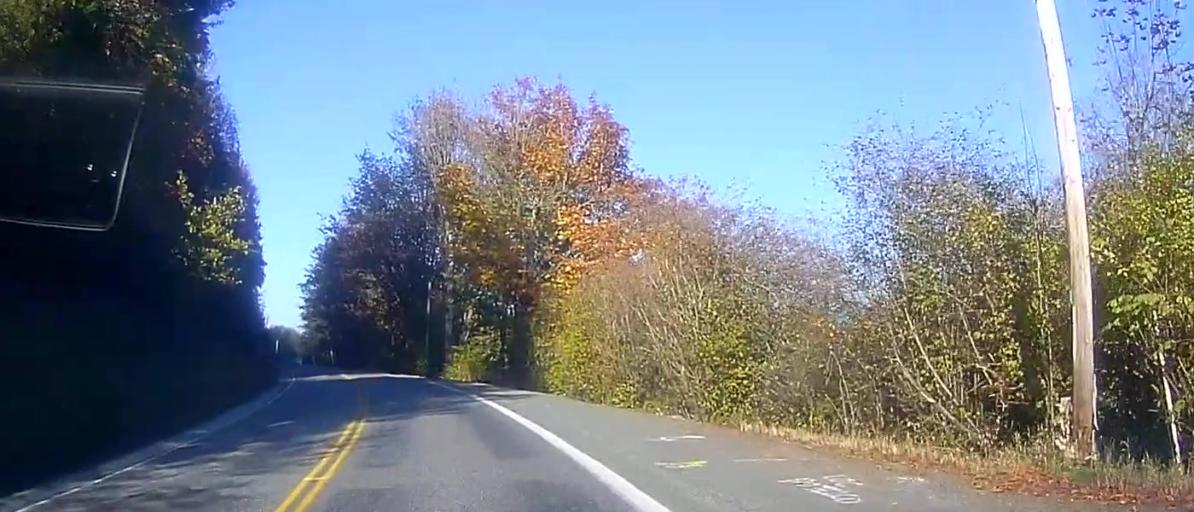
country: US
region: Washington
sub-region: Skagit County
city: Big Lake
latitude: 48.3987
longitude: -122.2430
